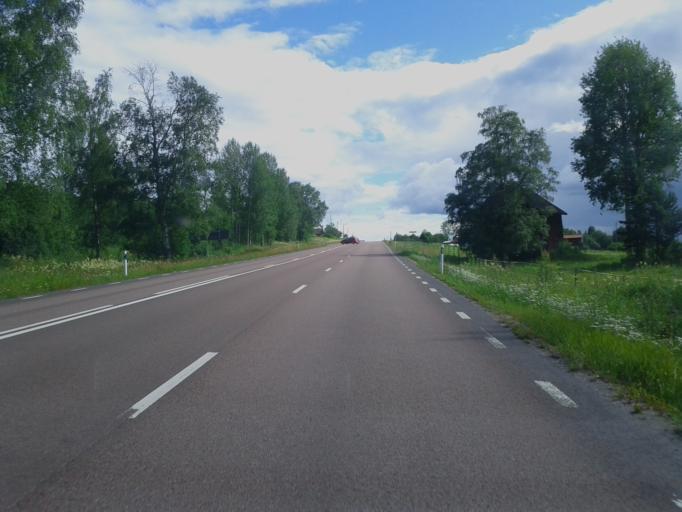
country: SE
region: Dalarna
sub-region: Rattviks Kommun
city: Raettvik
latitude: 60.8584
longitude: 15.1072
